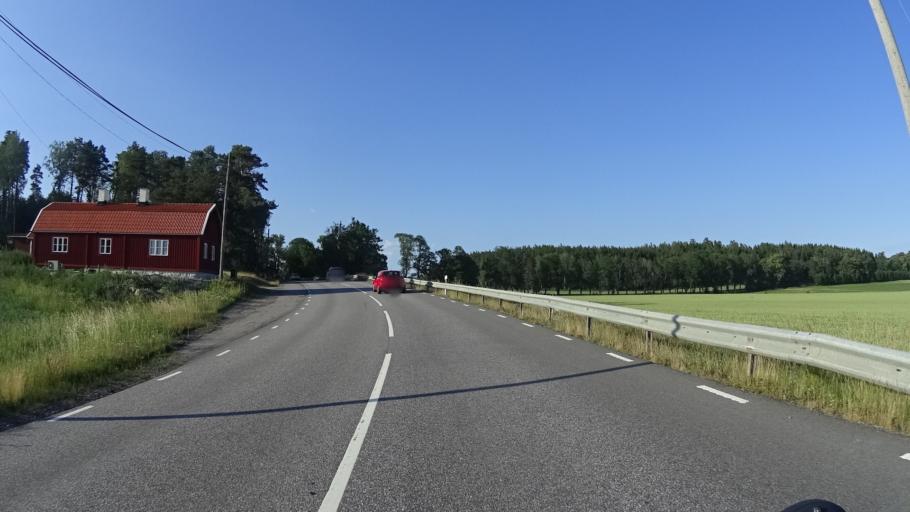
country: SE
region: Stockholm
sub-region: Sodertalje Kommun
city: Pershagen
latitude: 59.1103
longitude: 17.6423
